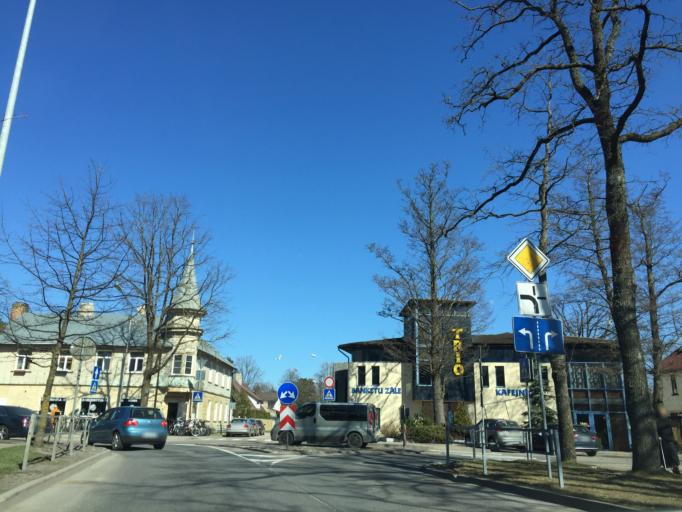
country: LV
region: Babite
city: Pinki
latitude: 56.9765
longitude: 23.8607
